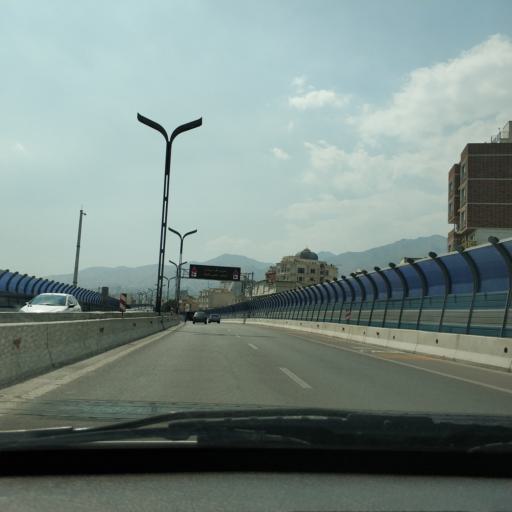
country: IR
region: Tehran
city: Tajrish
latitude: 35.7910
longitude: 51.4710
